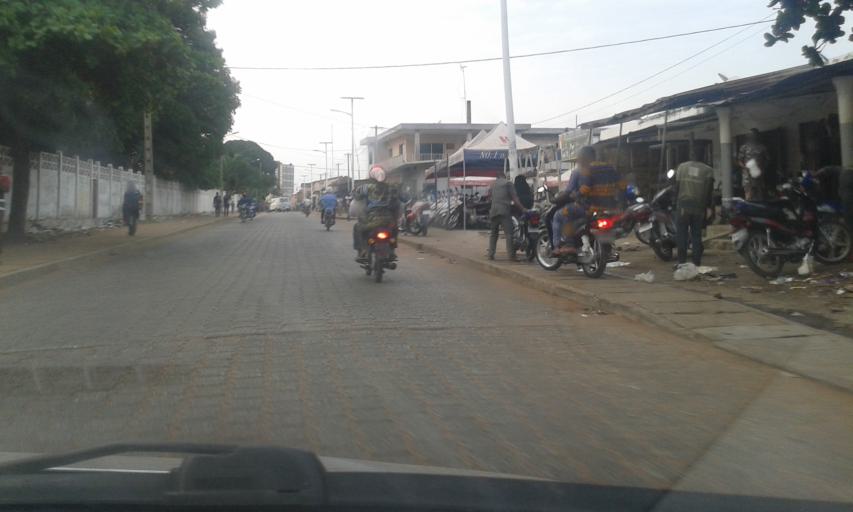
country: BJ
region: Queme
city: Porto-Novo
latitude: 6.4810
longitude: 2.6205
